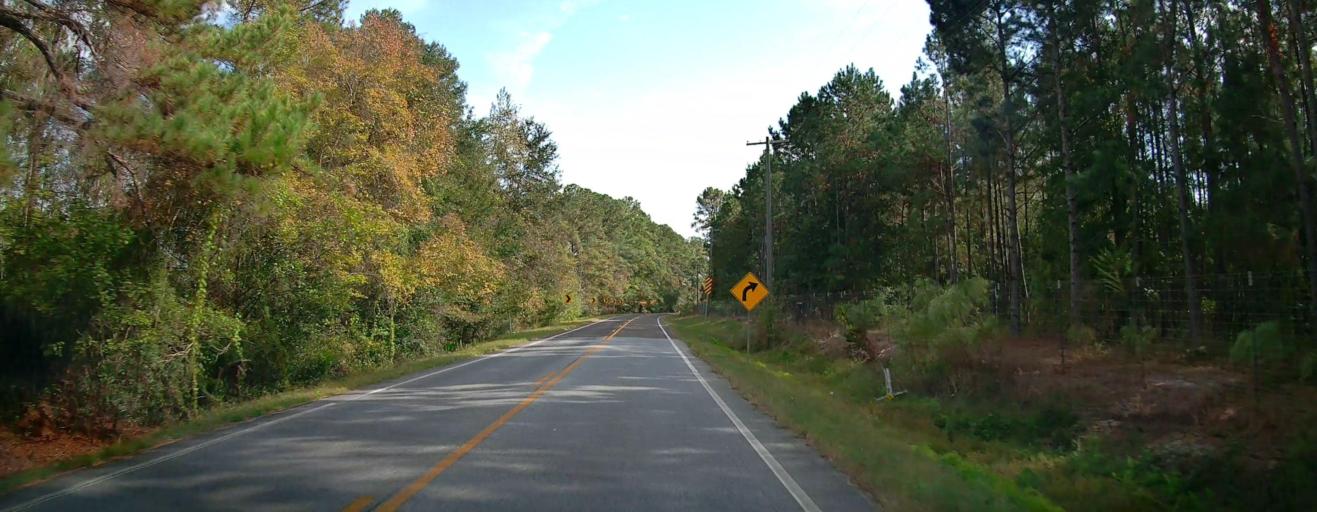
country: US
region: Georgia
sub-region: Thomas County
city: Thomasville
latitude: 30.9236
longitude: -84.0151
